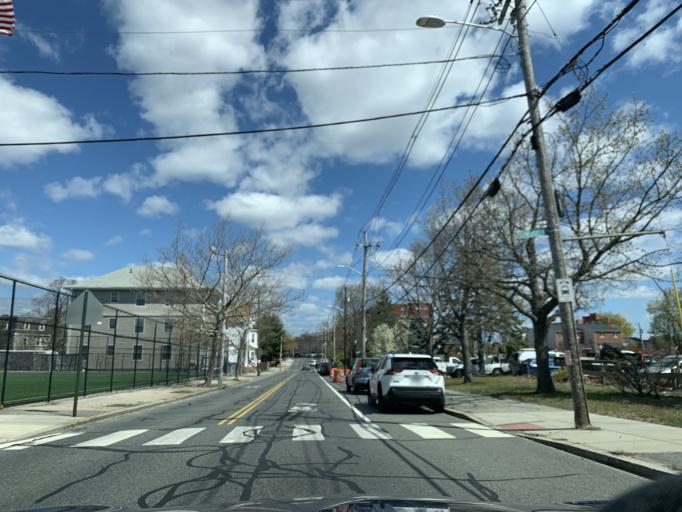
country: US
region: Rhode Island
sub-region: Providence County
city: Providence
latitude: 41.8108
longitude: -71.4155
